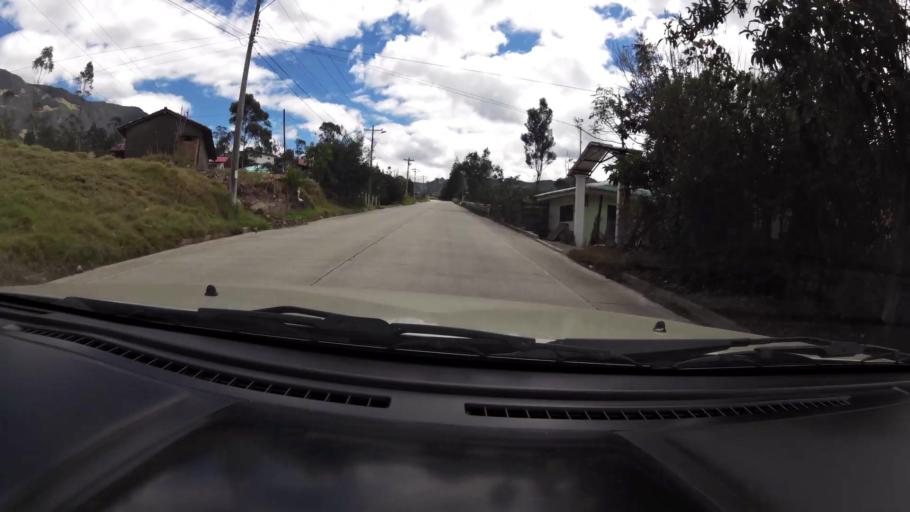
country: EC
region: Azuay
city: Cuenca
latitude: -3.1383
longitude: -79.1362
